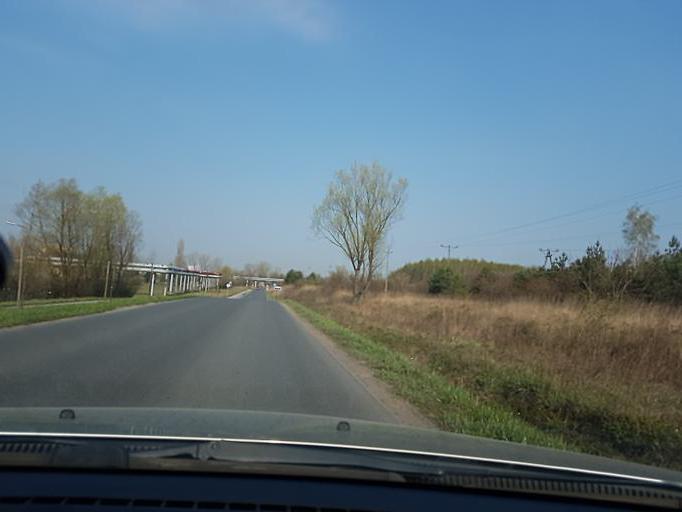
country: PL
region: Lodz Voivodeship
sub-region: Powiat kutnowski
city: Kutno
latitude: 52.2103
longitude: 19.4086
